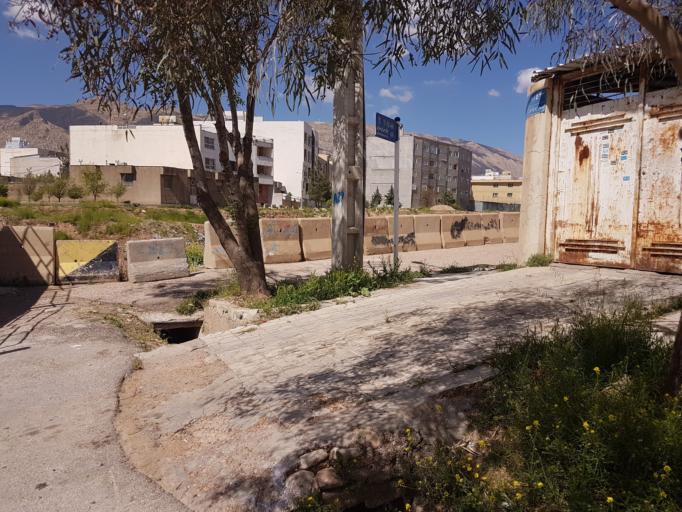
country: IR
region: Fars
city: Shiraz
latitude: 29.6890
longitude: 52.4615
